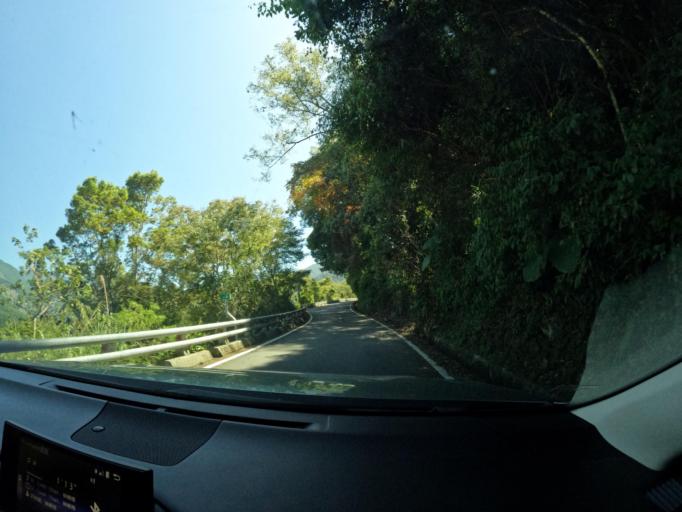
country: TW
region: Taiwan
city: Yujing
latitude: 23.2878
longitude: 120.8575
